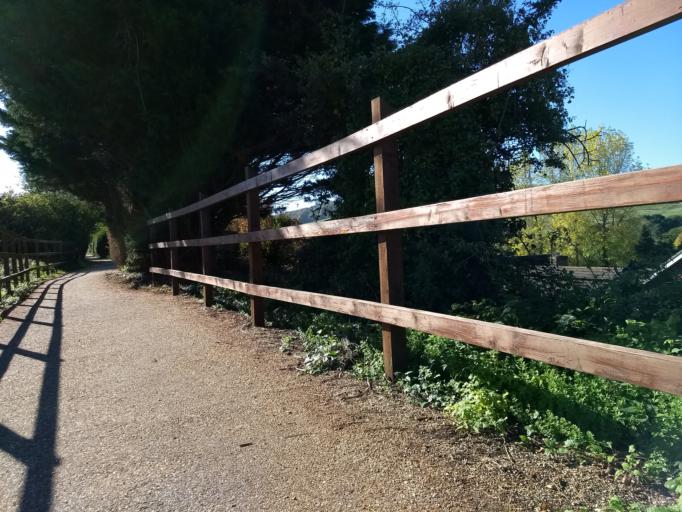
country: GB
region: England
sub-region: Isle of Wight
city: Ventnor
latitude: 50.6229
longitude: -1.2240
